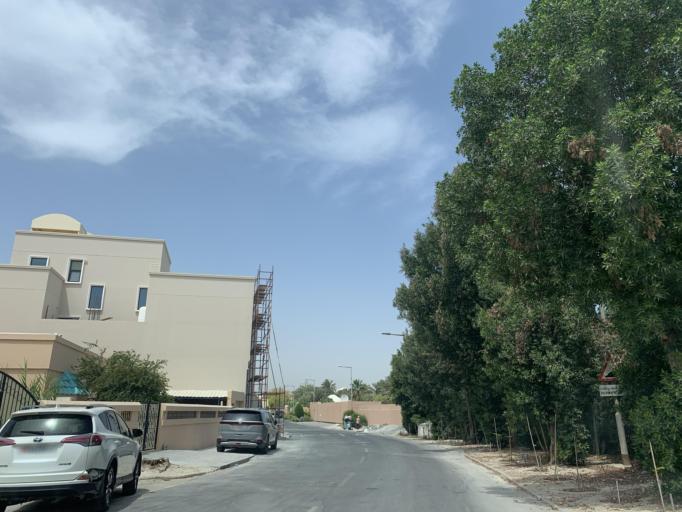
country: BH
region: Northern
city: Ar Rifa'
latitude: 26.1457
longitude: 50.5575
